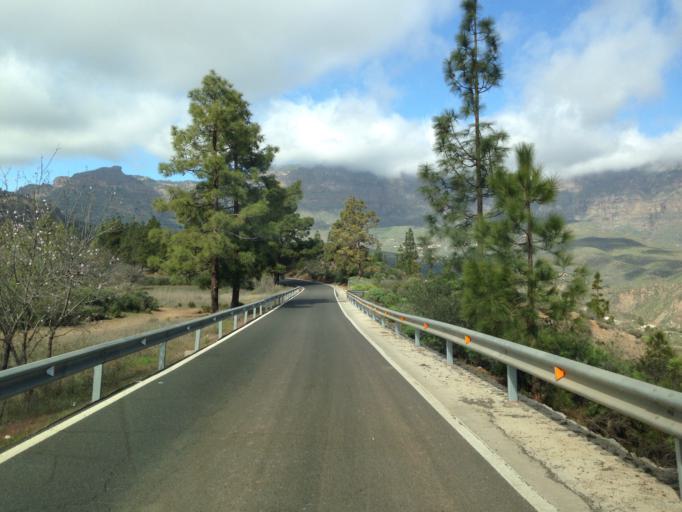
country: ES
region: Canary Islands
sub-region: Provincia de Las Palmas
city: San Bartolome
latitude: 27.9096
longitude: -15.5696
